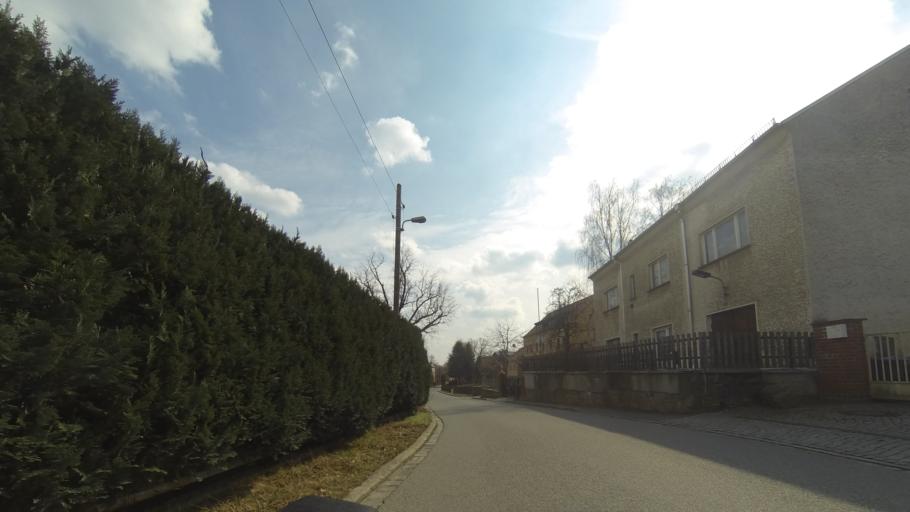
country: DE
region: Saxony
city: Albertstadt
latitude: 51.1165
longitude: 13.7612
